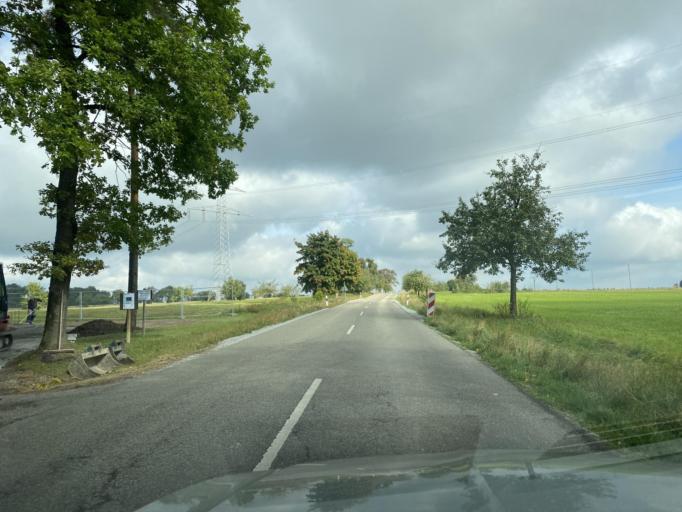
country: DE
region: Baden-Wuerttemberg
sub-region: Regierungsbezirk Stuttgart
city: Buhlertann
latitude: 49.0461
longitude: 9.9589
